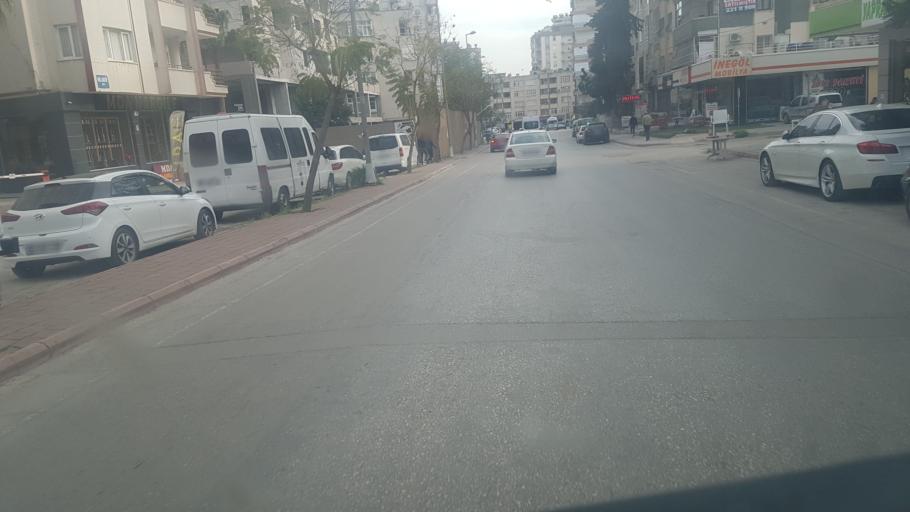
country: TR
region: Adana
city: Adana
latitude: 37.0285
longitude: 35.3104
